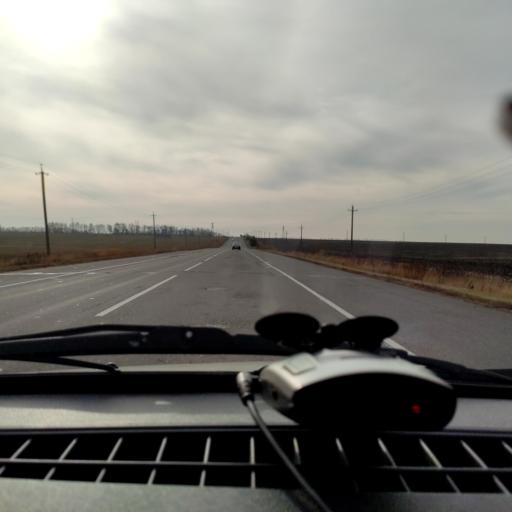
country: RU
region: Voronezj
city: Strelitsa
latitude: 51.5532
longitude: 38.9722
